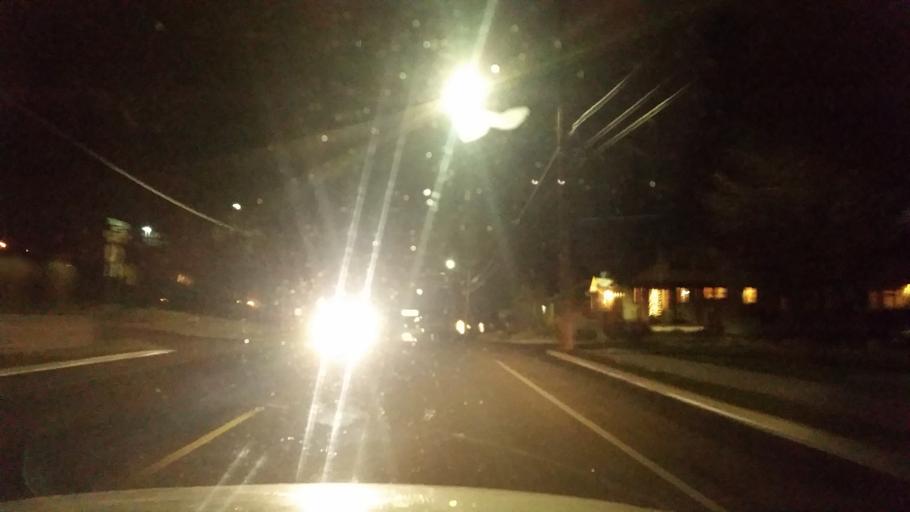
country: US
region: Washington
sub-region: Spokane County
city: Spokane
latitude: 47.6378
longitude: -117.4167
